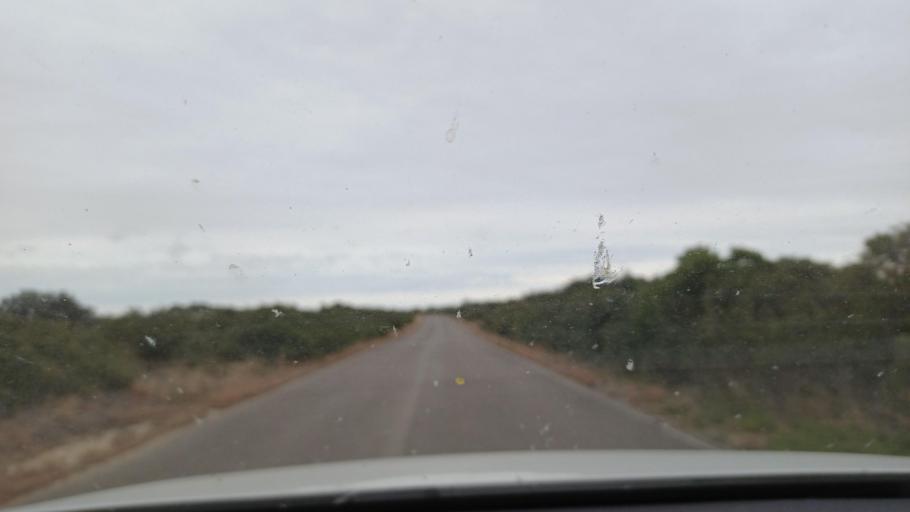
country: ES
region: Valencia
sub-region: Provincia de Castello
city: Canet lo Roig
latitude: 40.5885
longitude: 0.2831
